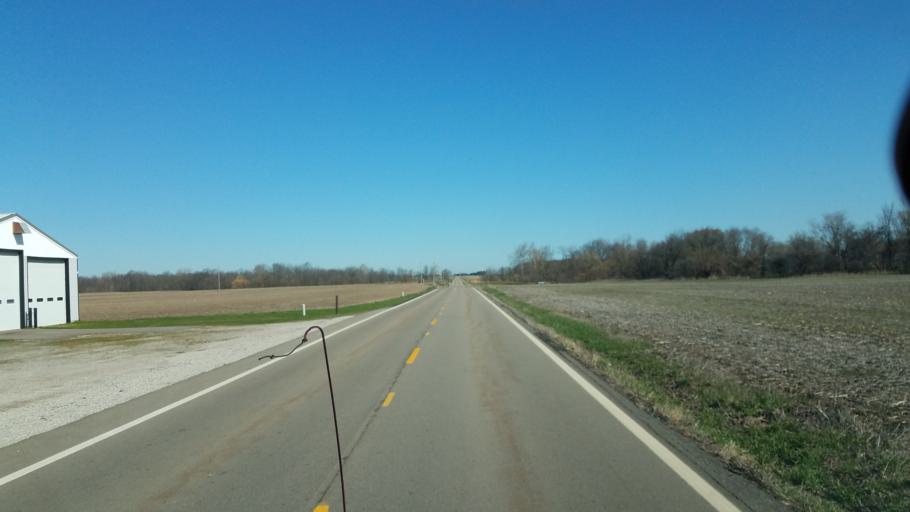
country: US
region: Ohio
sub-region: Richland County
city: Shelby
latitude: 40.9286
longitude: -82.7721
